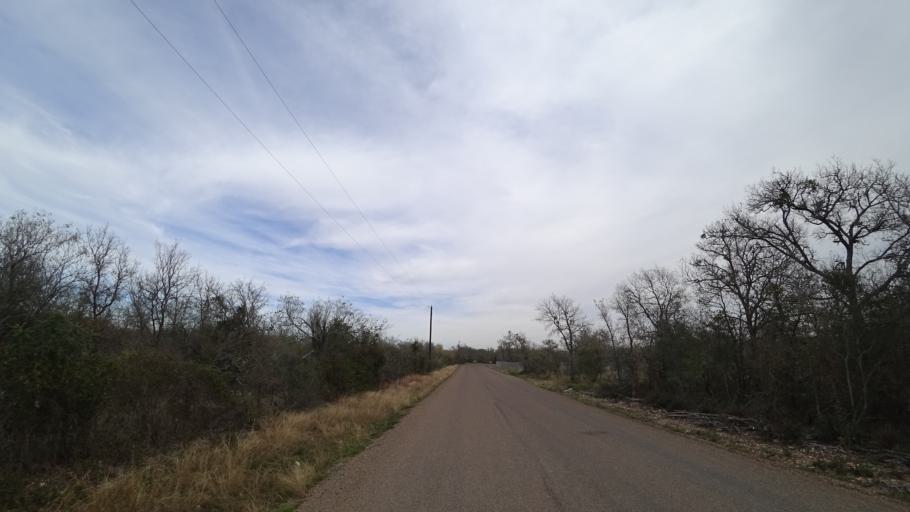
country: US
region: Texas
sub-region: Travis County
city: Garfield
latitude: 30.1131
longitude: -97.5690
